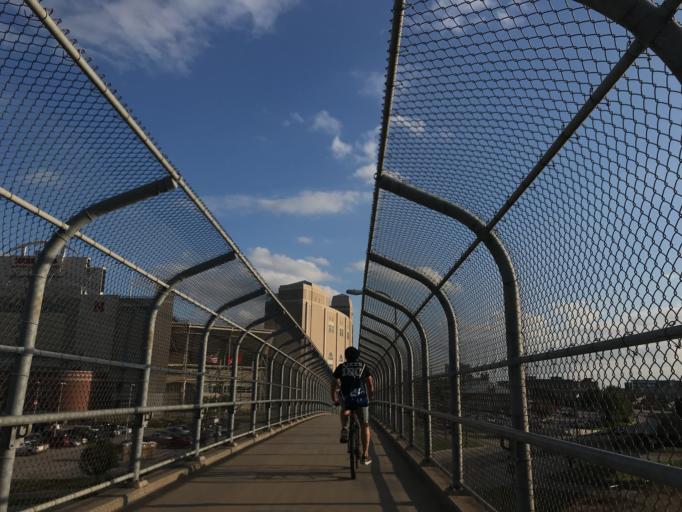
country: US
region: Nebraska
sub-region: Lancaster County
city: Lincoln
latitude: 40.8234
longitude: -96.7070
